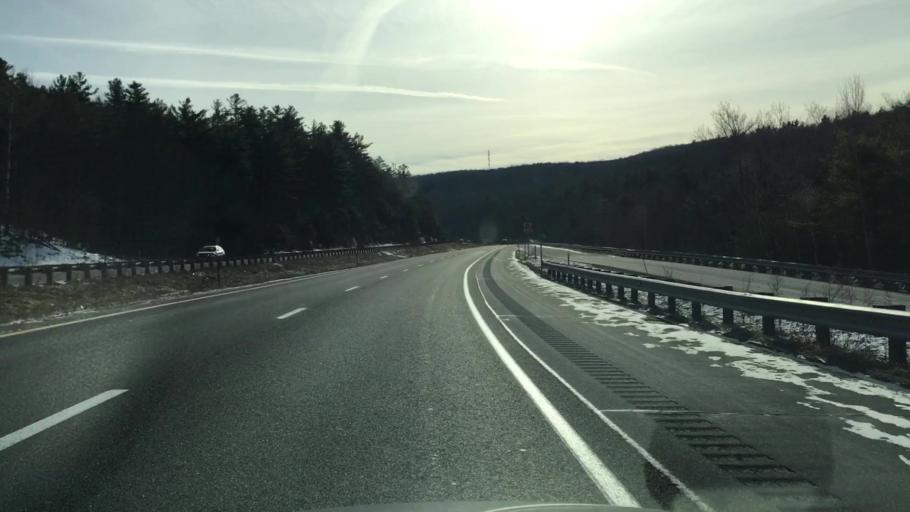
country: US
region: New Hampshire
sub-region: Grafton County
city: Enfield
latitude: 43.5963
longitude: -72.1658
